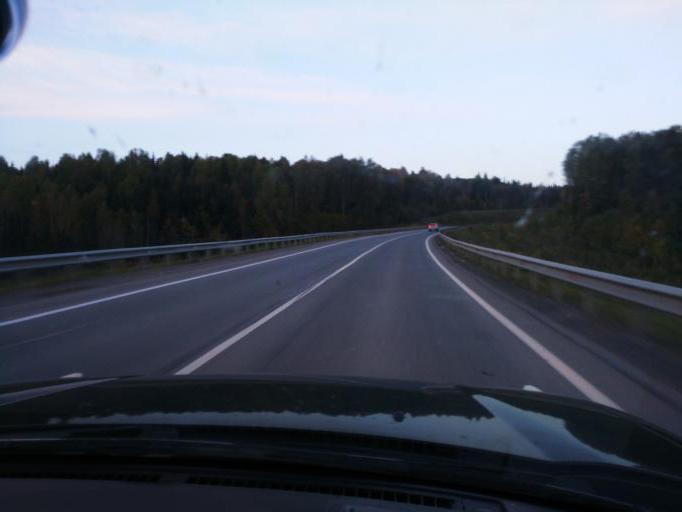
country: RU
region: Perm
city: Sylva
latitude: 58.3017
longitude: 56.7776
